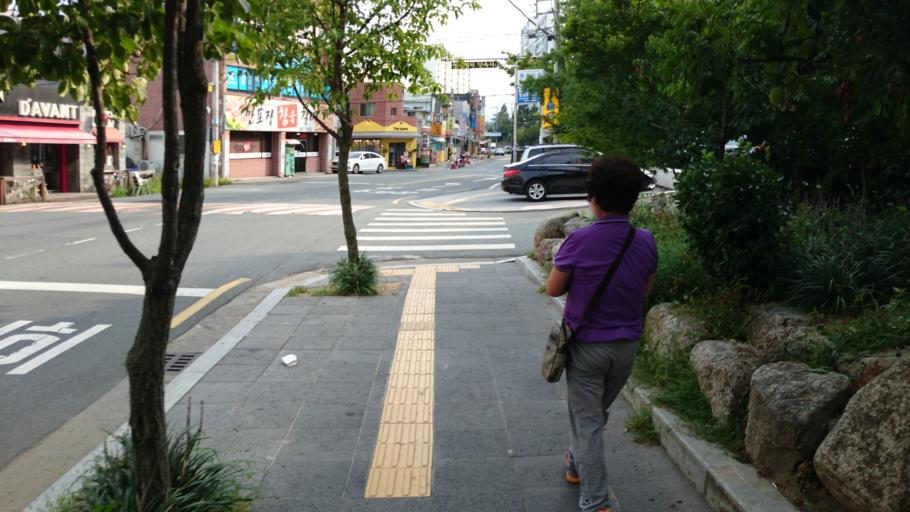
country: KR
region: Daegu
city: Daegu
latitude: 35.8820
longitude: 128.6624
